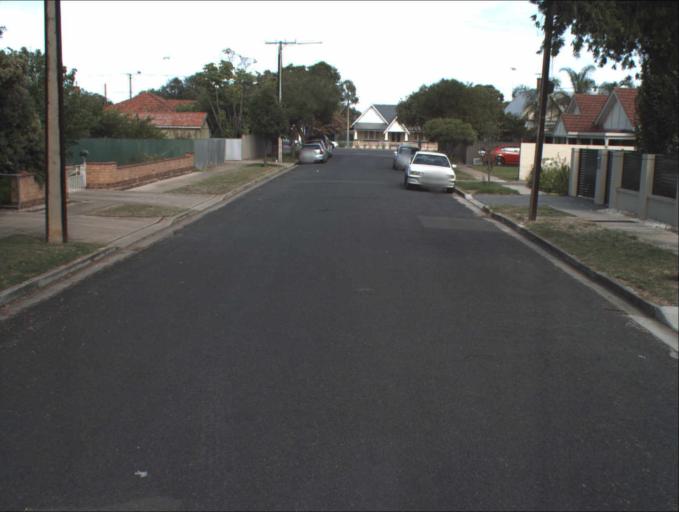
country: AU
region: South Australia
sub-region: Port Adelaide Enfield
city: Klemzig
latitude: -34.8781
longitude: 138.6206
